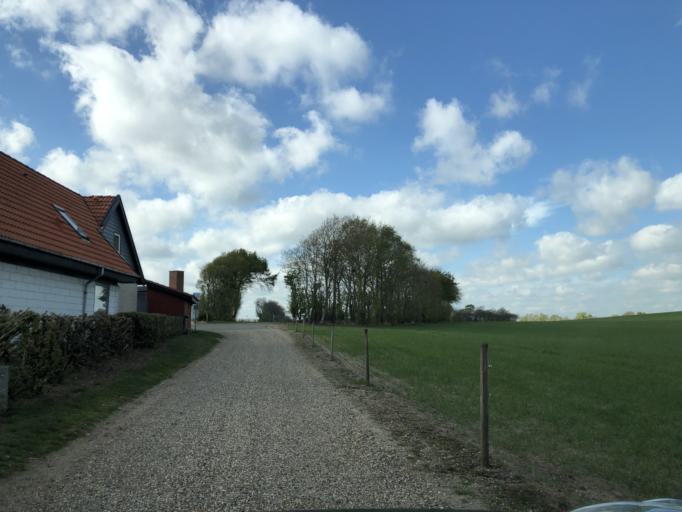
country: DK
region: Central Jutland
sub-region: Herning Kommune
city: Avlum
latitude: 56.2969
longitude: 8.7413
